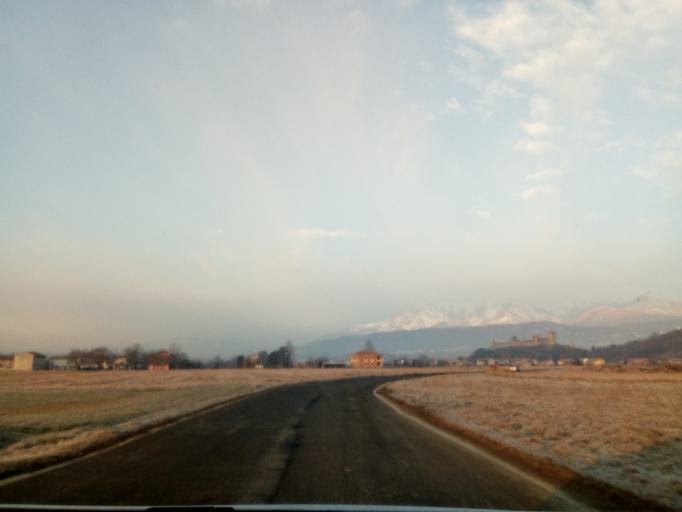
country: IT
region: Piedmont
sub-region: Provincia di Torino
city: Pavone Canavese
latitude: 45.4325
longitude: 7.8688
